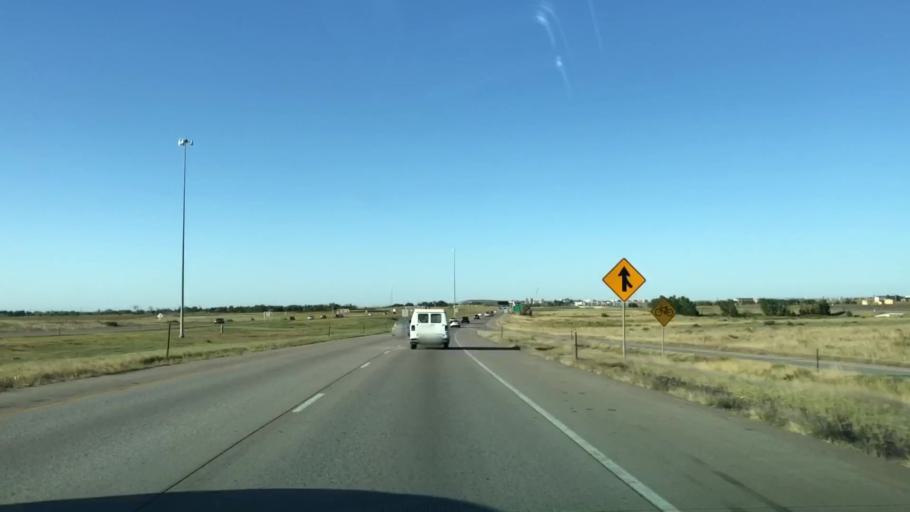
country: US
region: Colorado
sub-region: Adams County
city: Aurora
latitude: 39.7870
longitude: -104.7900
